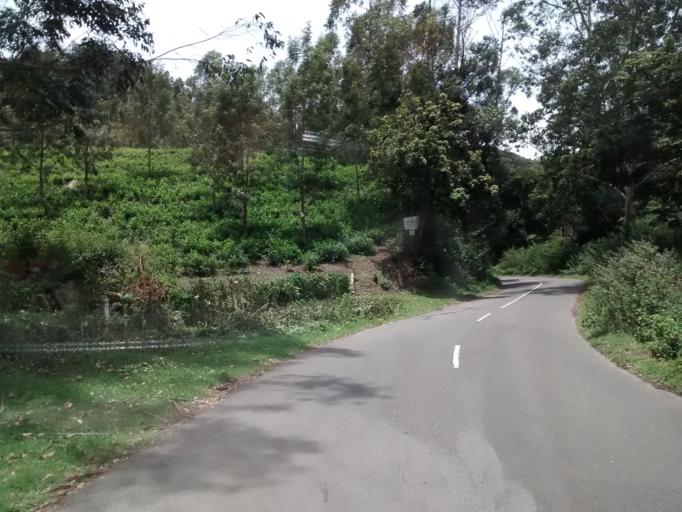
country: IN
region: Kerala
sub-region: Idukki
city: Munnar
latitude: 10.1372
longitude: 77.2053
